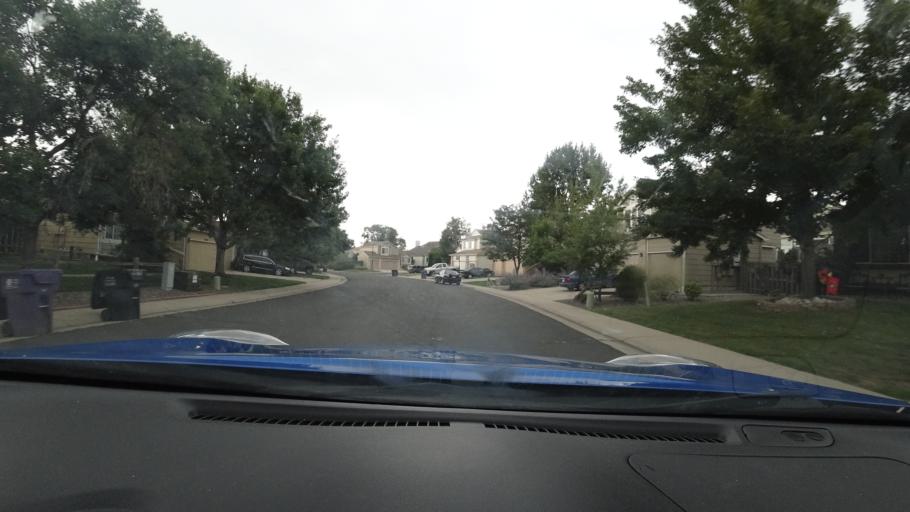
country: US
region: Colorado
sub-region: Adams County
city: Aurora
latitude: 39.7770
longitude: -104.7507
